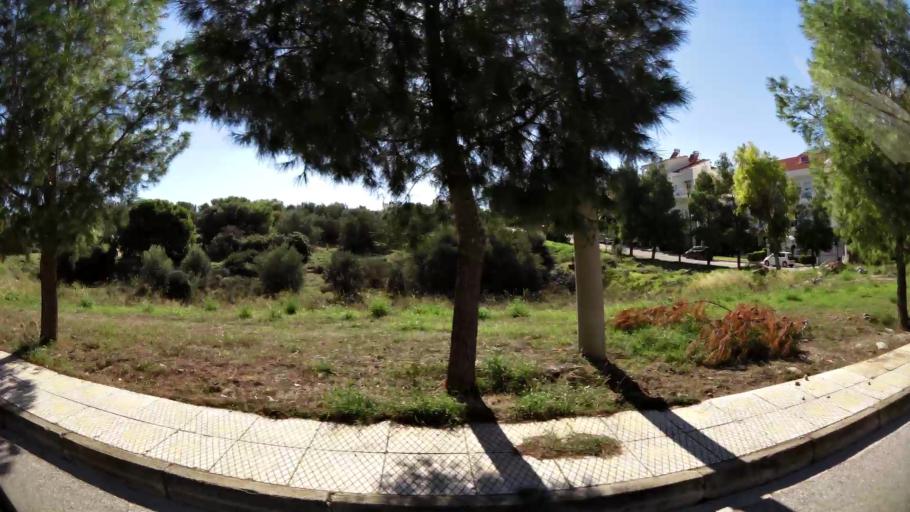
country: GR
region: Attica
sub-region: Nomarchia Anatolikis Attikis
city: Voula
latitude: 37.8426
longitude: 23.7794
